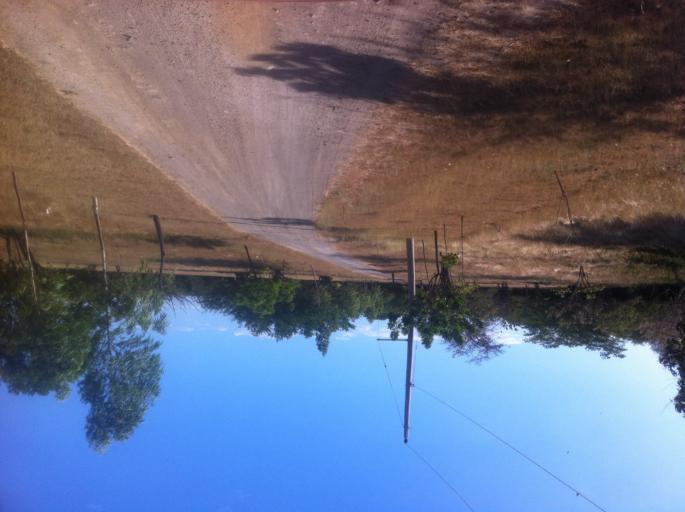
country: NI
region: Managua
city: Carlos Fonseca Amador
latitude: 11.9011
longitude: -86.6075
